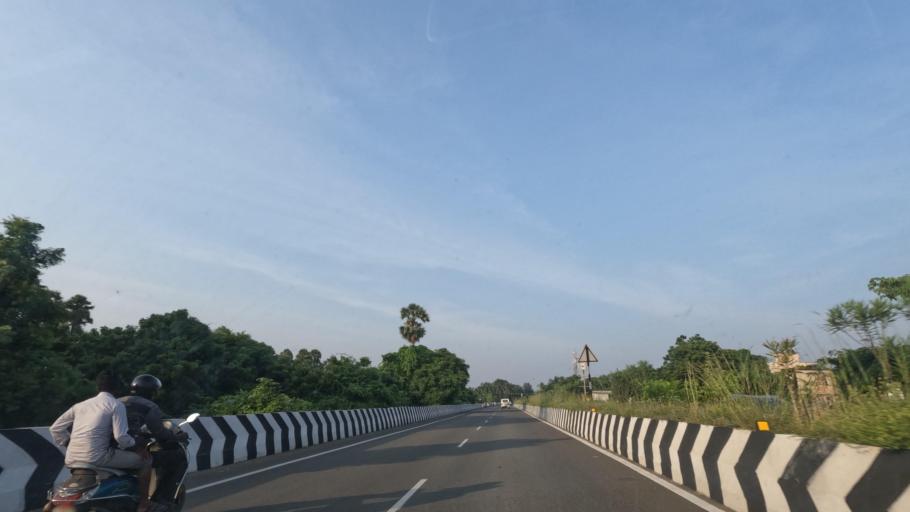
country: IN
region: Tamil Nadu
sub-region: Kancheepuram
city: Mamallapuram
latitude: 12.6497
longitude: 80.2038
